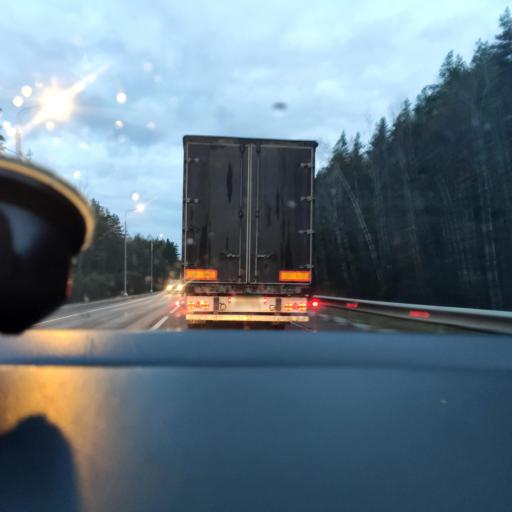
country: RU
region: Moskovskaya
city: Yegor'yevsk
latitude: 55.4499
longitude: 39.0057
